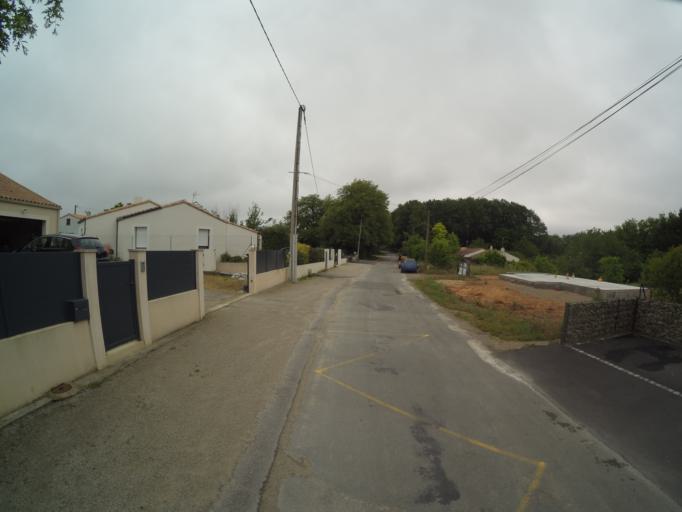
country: FR
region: Pays de la Loire
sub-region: Departement de la Vendee
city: La Roche-sur-Yon
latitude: 46.6340
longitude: -1.4278
